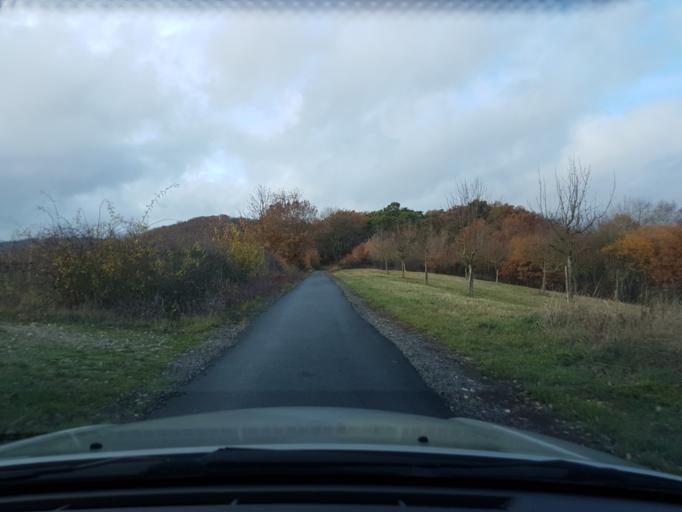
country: DE
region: Hesse
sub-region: Regierungsbezirk Darmstadt
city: Kiedrich
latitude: 50.0364
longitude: 8.0519
